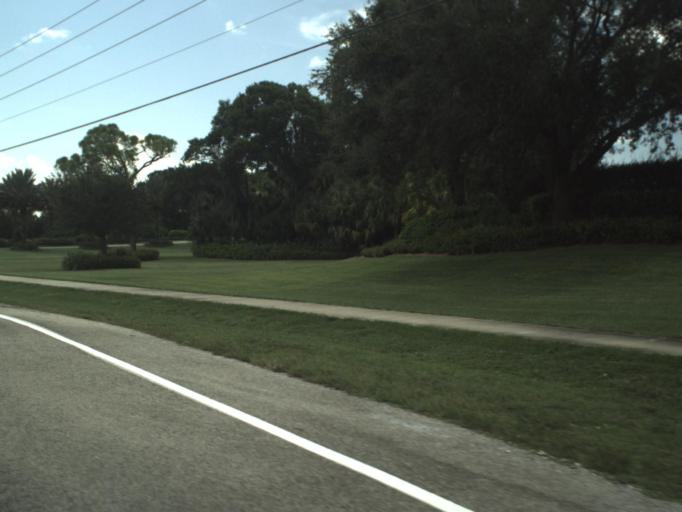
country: US
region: Florida
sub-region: Martin County
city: Port Salerno
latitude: 27.1195
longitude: -80.1823
